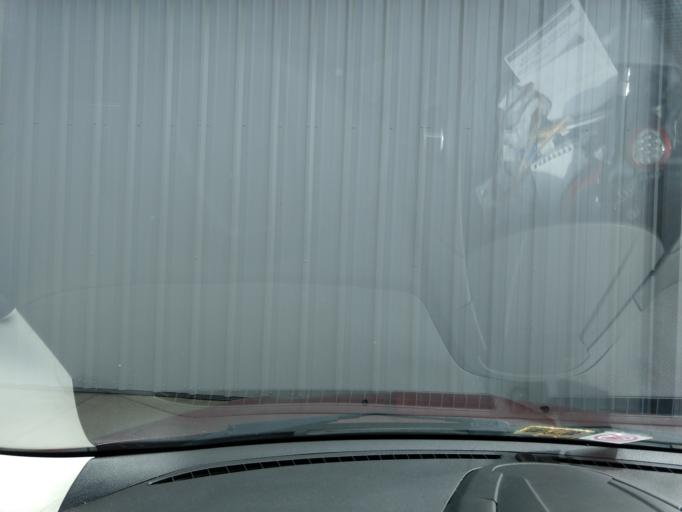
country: US
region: West Virginia
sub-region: Randolph County
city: Elkins
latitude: 38.8855
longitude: -79.8441
